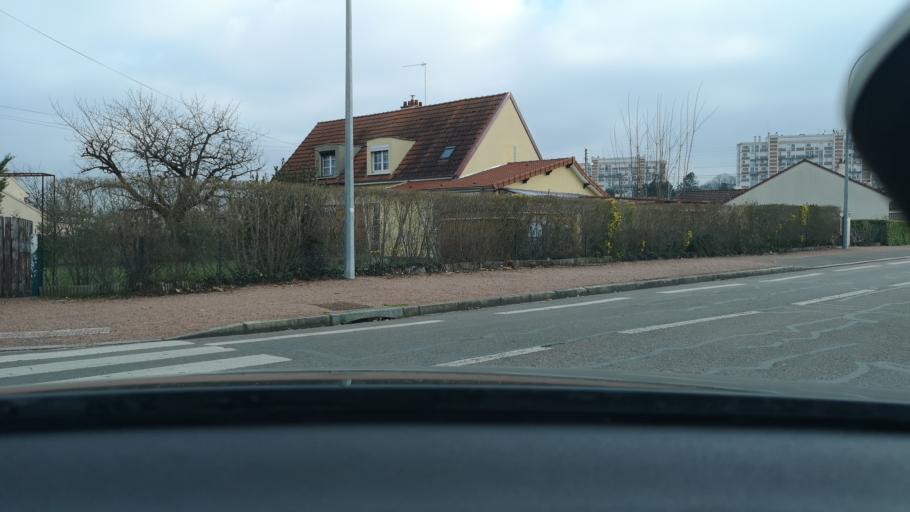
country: FR
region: Bourgogne
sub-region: Departement de Saone-et-Loire
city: Chalon-sur-Saone
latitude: 46.7980
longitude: 4.8402
